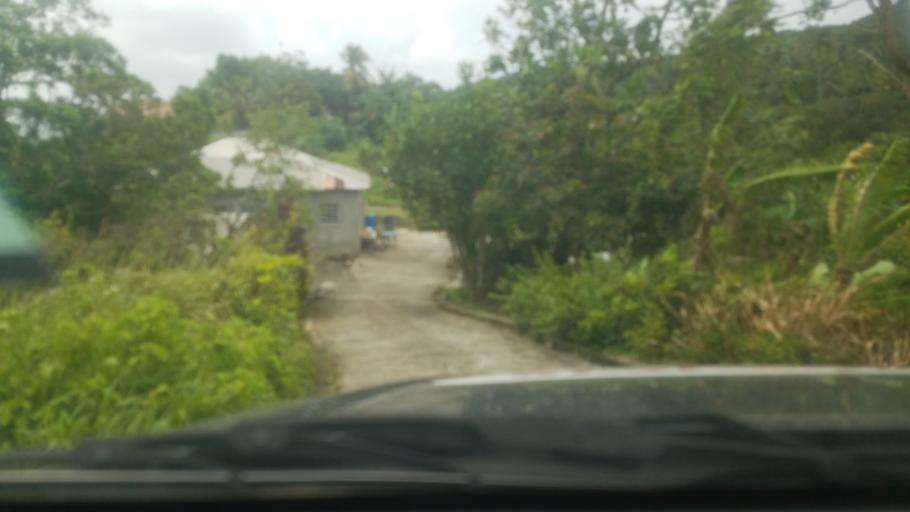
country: LC
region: Laborie Quarter
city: Laborie
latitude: 13.7745
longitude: -61.0043
